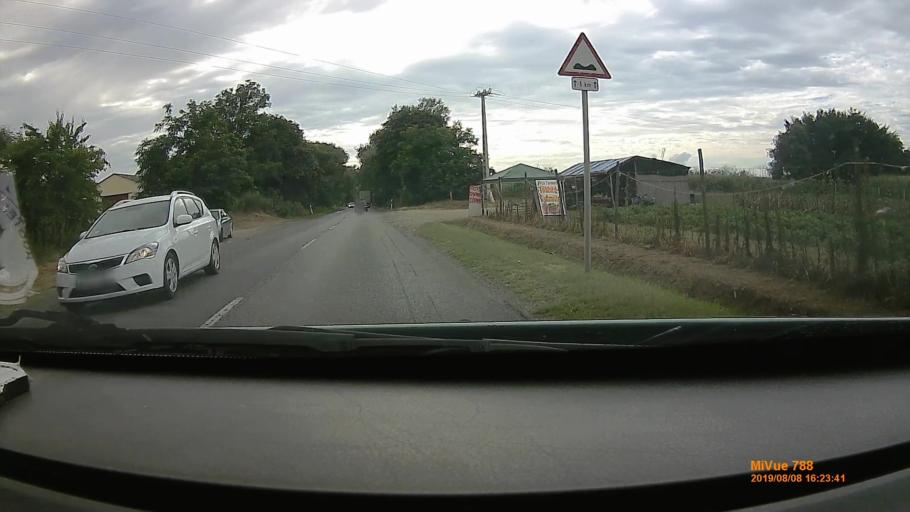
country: HU
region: Szabolcs-Szatmar-Bereg
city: Nyirmeggyes
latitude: 47.9689
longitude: 22.2375
